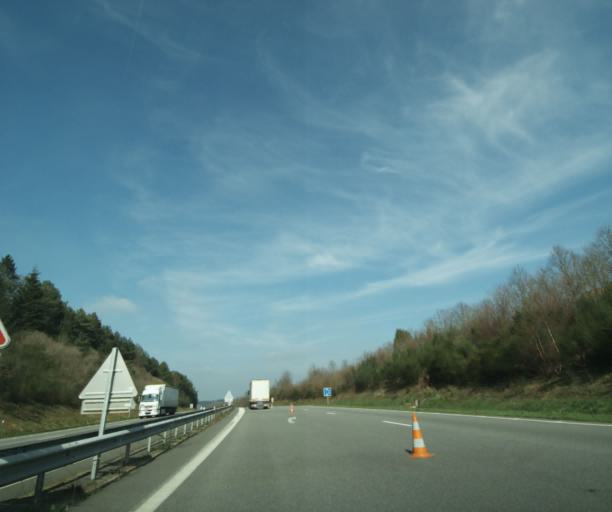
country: FR
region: Limousin
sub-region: Departement de la Haute-Vienne
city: Razes
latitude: 46.0575
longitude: 1.3604
